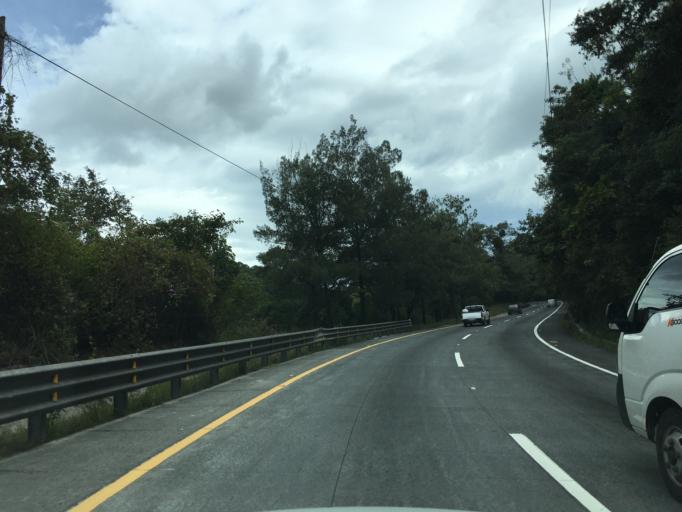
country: GT
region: Sacatepequez
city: Santa Lucia Milpas Altas
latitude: 14.5683
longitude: -90.6851
